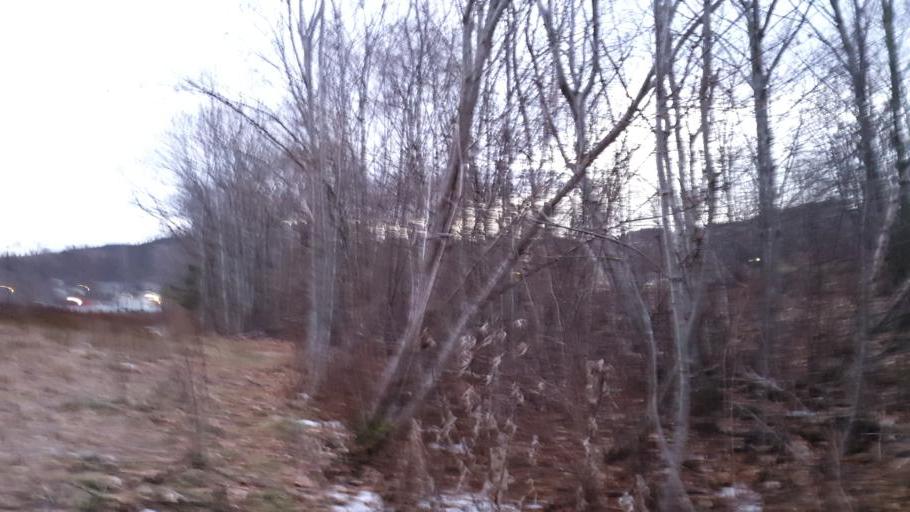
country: NO
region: Sor-Trondelag
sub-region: Trondheim
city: Trondheim
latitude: 63.4302
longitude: 10.5334
